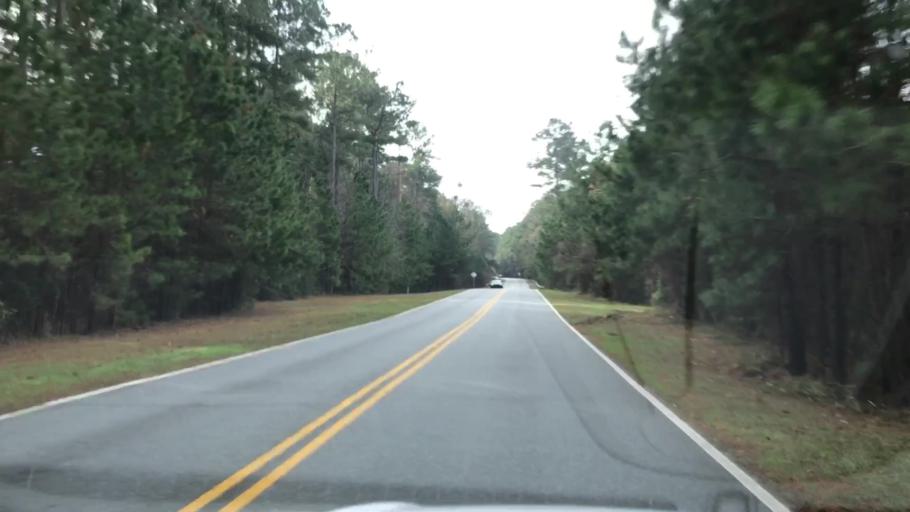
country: US
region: South Carolina
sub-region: Beaufort County
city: Bluffton
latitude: 32.2829
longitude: -80.9274
